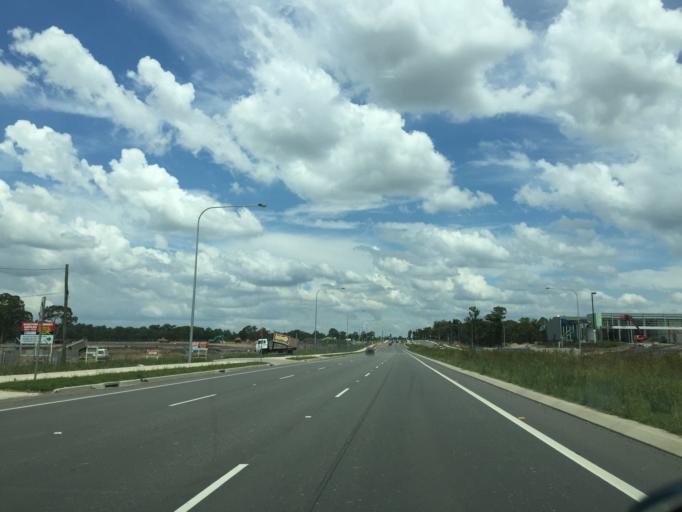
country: AU
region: New South Wales
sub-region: Blacktown
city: Hassall Grove
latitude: -33.7199
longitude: 150.8443
